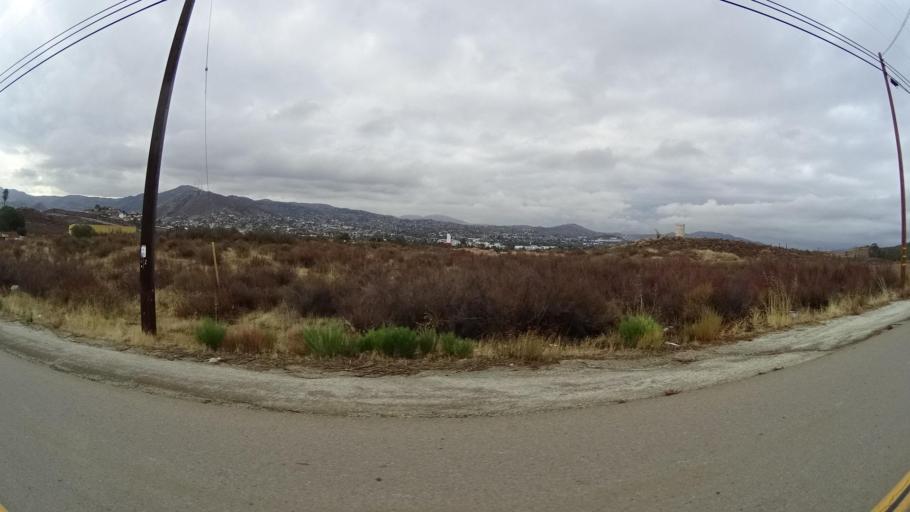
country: MX
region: Baja California
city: Tecate
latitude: 32.5827
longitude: -116.6287
